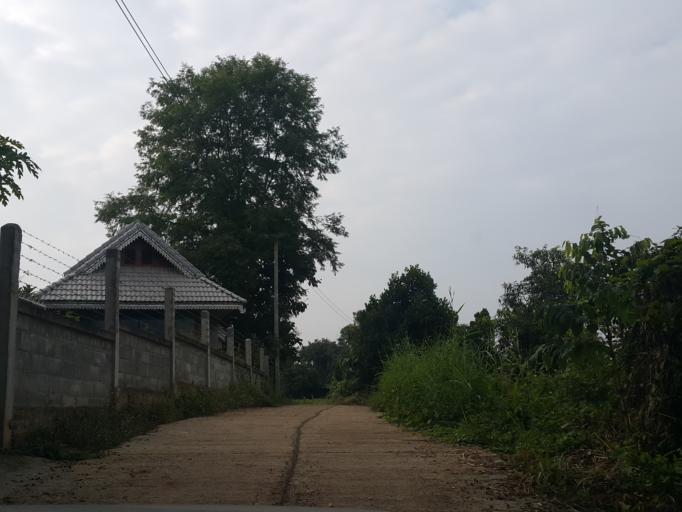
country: TH
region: Mae Hong Son
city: Wiang Nuea
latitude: 19.3717
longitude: 98.4469
